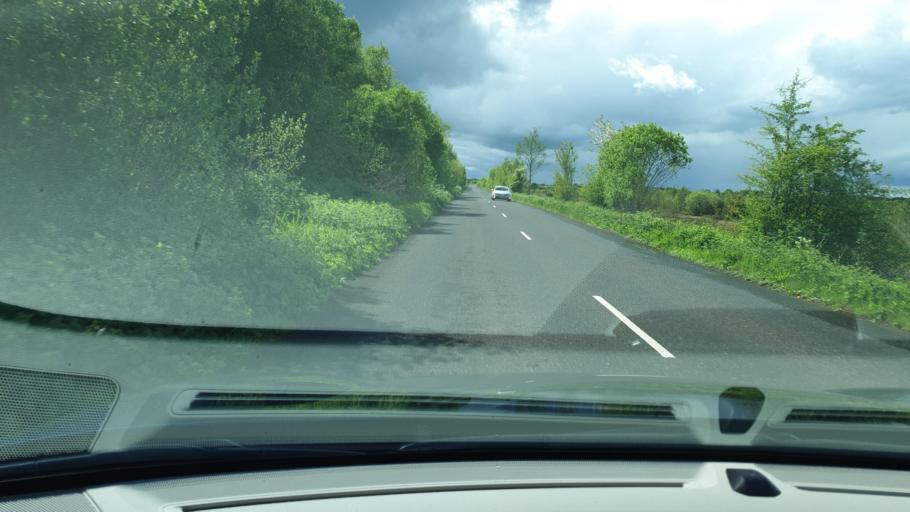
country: IE
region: Leinster
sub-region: Uibh Fhaili
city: Clara
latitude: 53.2373
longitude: -7.6788
